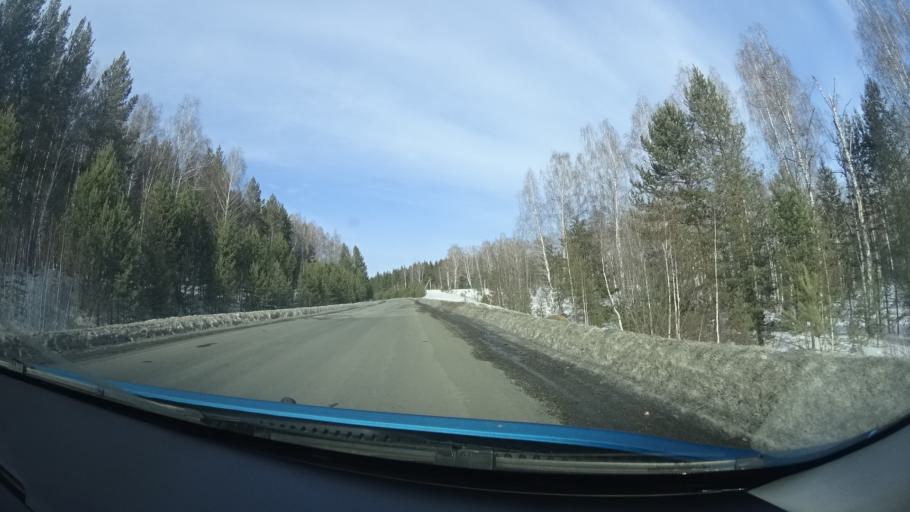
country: RU
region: Bashkortostan
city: Lomovka
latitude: 53.8248
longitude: 58.2810
